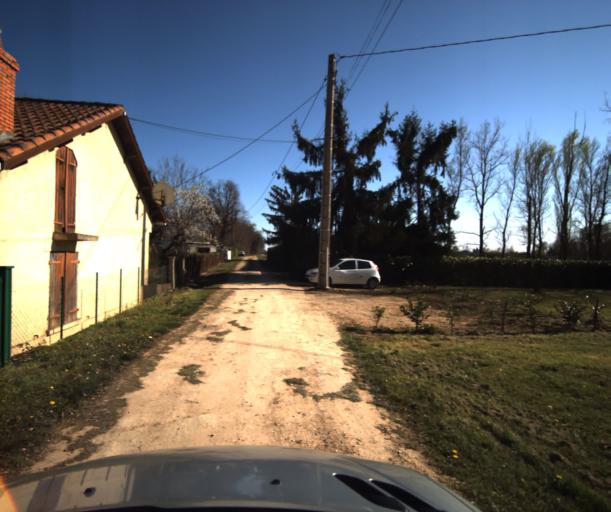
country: FR
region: Midi-Pyrenees
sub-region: Departement du Tarn-et-Garonne
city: Bressols
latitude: 43.9623
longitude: 1.3458
